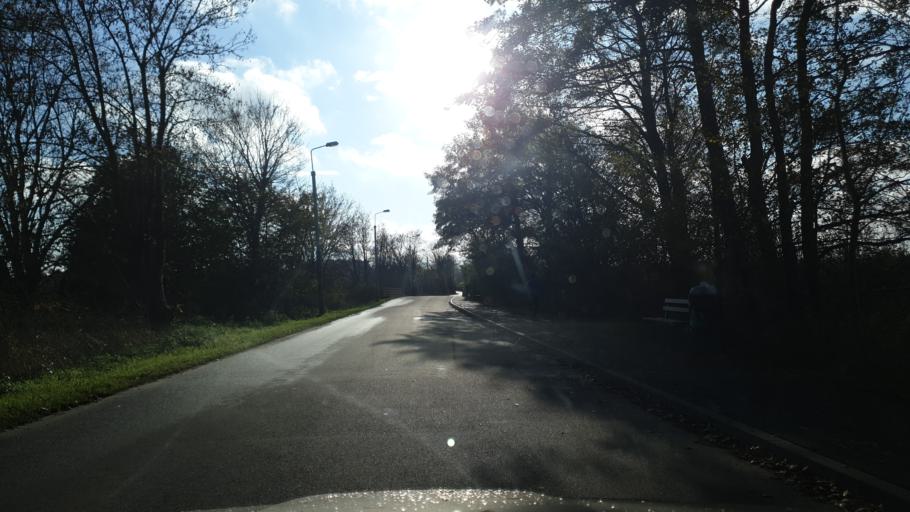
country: PL
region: Pomeranian Voivodeship
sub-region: Powiat pucki
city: Jastrzebia Gora
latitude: 54.8293
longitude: 18.2444
